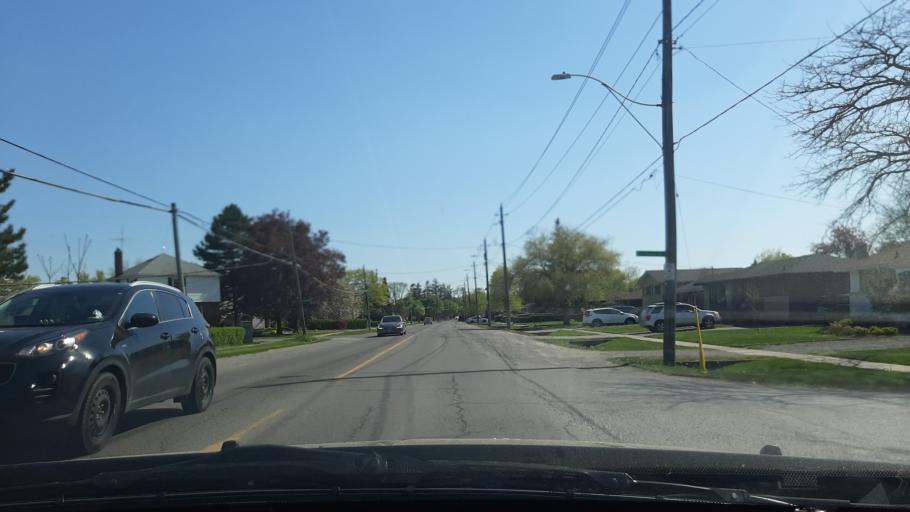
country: CA
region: Ontario
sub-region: Regional Municipality of Niagara
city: St. Catharines
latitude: 43.2056
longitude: -79.2200
